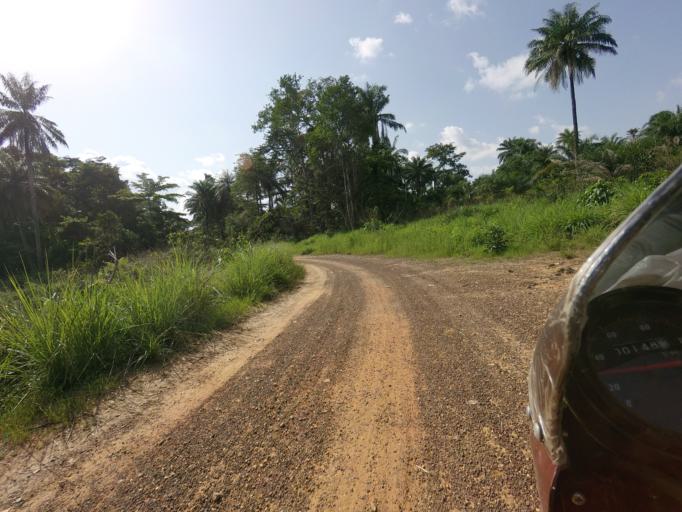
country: SL
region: Eastern Province
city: Kailahun
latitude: 8.3565
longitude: -10.7120
